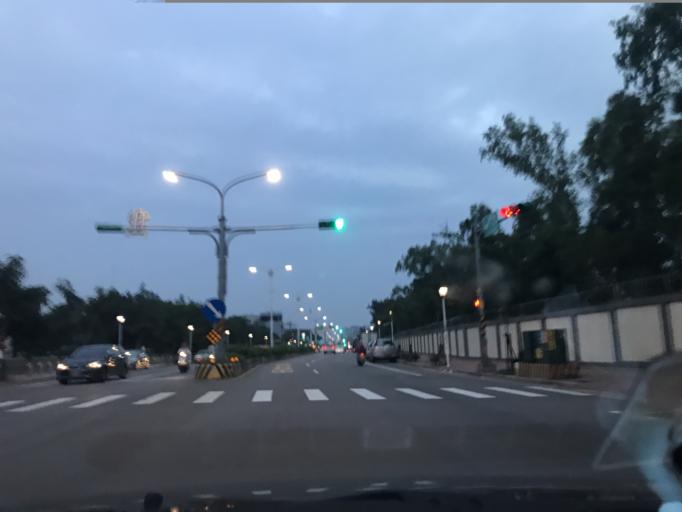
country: TW
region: Taiwan
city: Daxi
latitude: 24.9299
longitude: 121.2401
